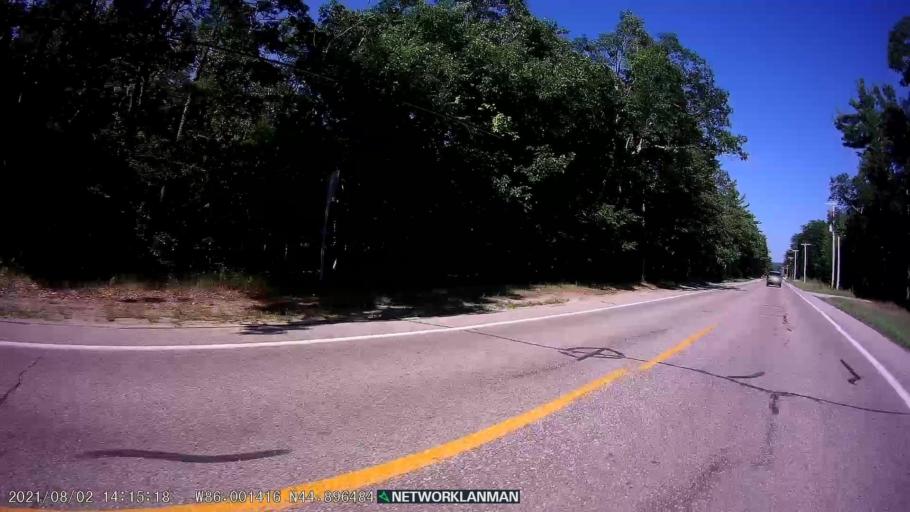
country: US
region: Michigan
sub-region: Leelanau County
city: Leland
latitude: 44.8965
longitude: -86.0012
